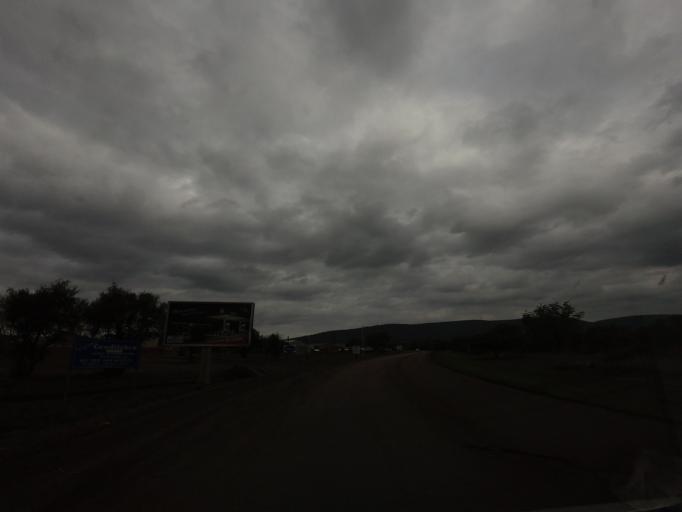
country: ZA
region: Mpumalanga
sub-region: Ehlanzeni District
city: Komatipoort
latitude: -25.4451
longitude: 31.9461
